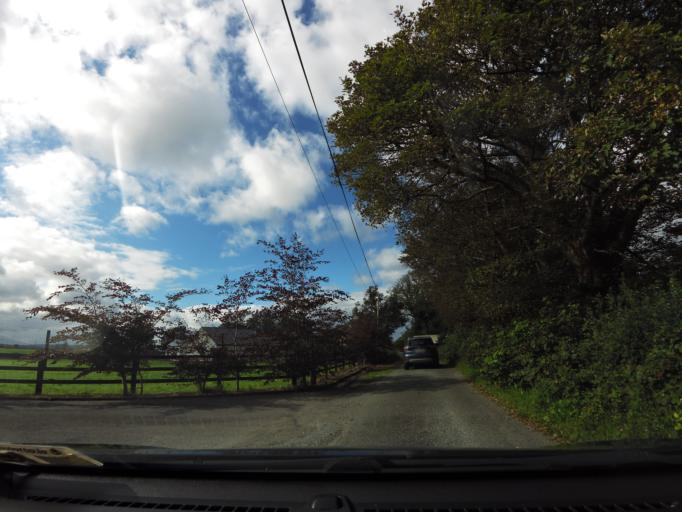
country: IE
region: Connaught
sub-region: County Galway
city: Moycullen
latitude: 53.3507
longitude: -9.1588
